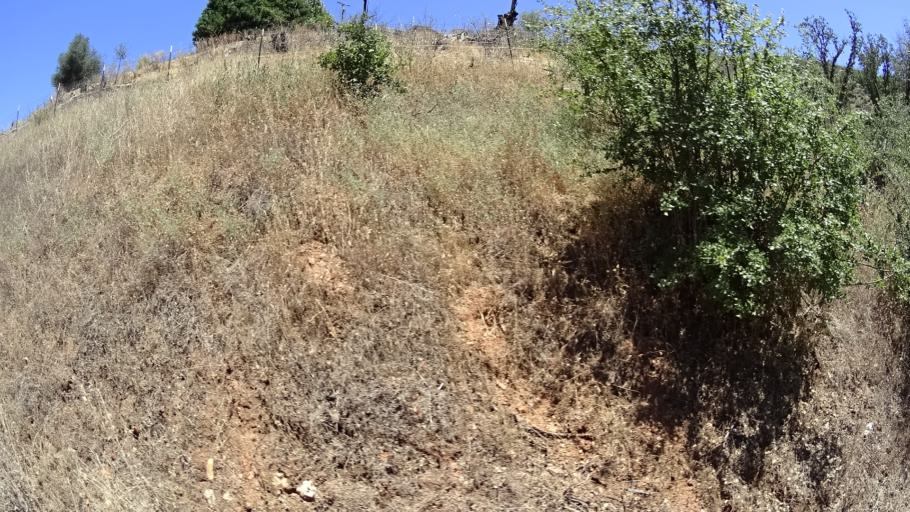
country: US
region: California
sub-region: Calaveras County
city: San Andreas
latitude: 38.2834
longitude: -120.6700
